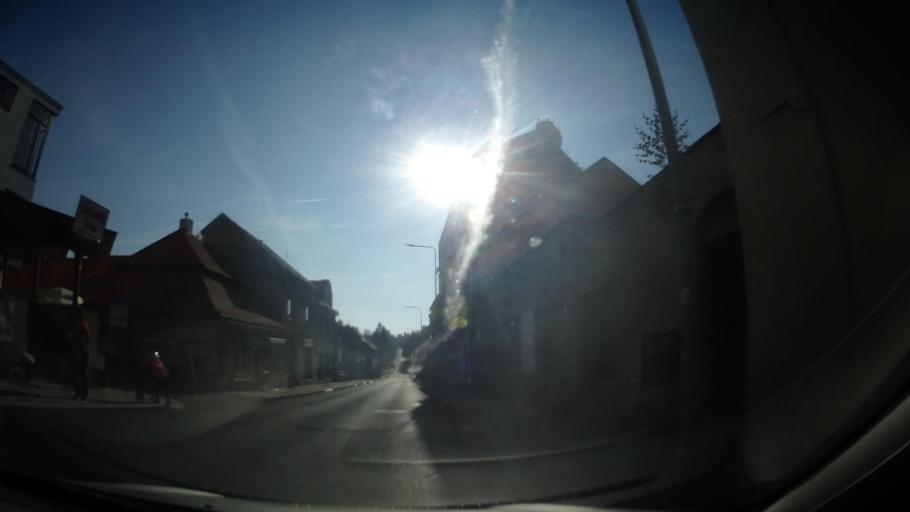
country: CZ
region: Central Bohemia
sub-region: Okres Praha-Vychod
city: Ricany
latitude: 49.9916
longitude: 14.6571
